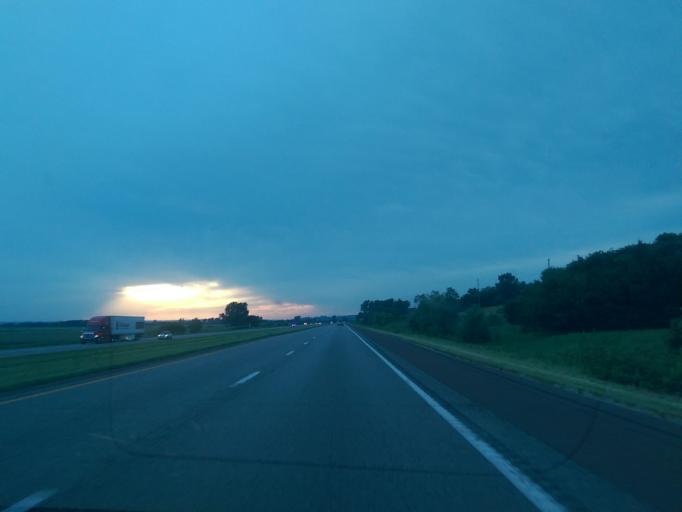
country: US
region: Missouri
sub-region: Holt County
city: Mound City
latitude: 40.1648
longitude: -95.2871
